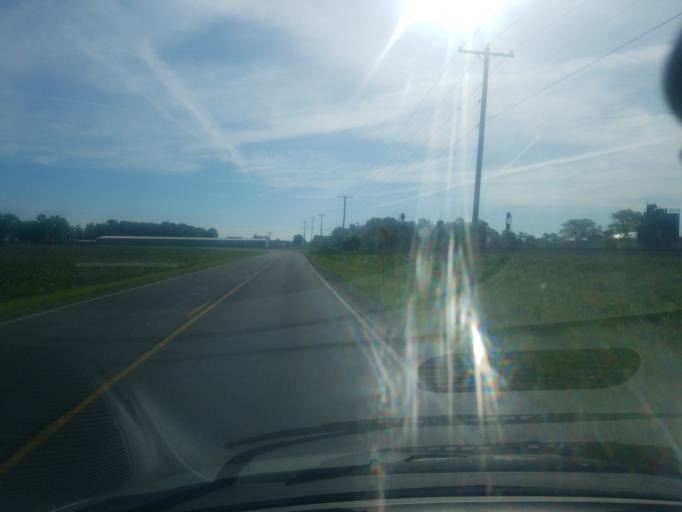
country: US
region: Ohio
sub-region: Marion County
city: Marion
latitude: 40.6040
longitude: -83.0765
